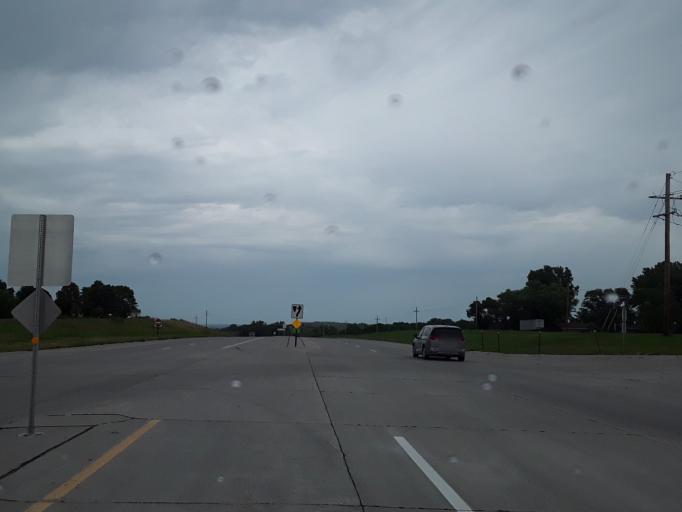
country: US
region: Nebraska
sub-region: Washington County
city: Blair
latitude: 41.5015
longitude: -96.1472
